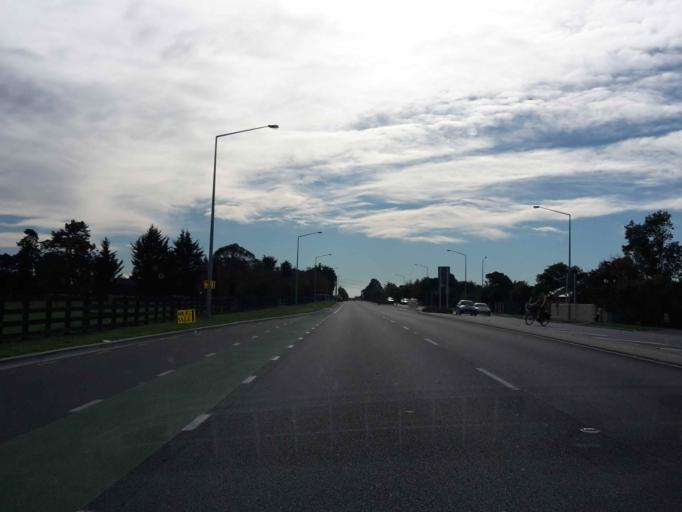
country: NZ
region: Canterbury
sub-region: Selwyn District
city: Prebbleton
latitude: -43.5187
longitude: 172.5349
